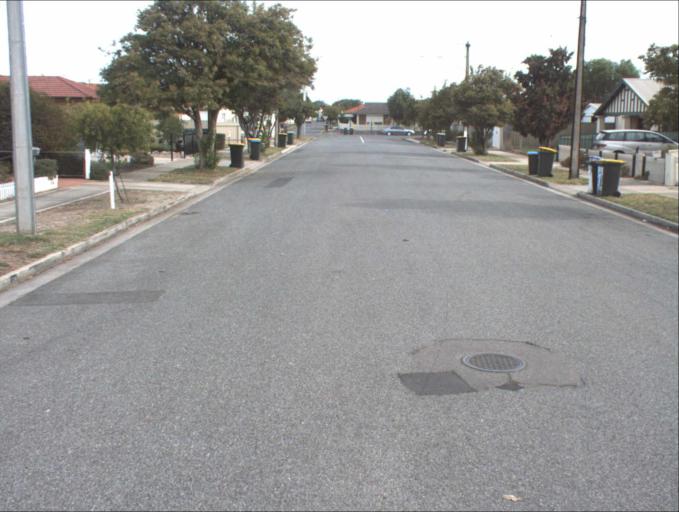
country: AU
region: South Australia
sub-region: Port Adelaide Enfield
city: Birkenhead
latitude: -34.8310
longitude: 138.4942
